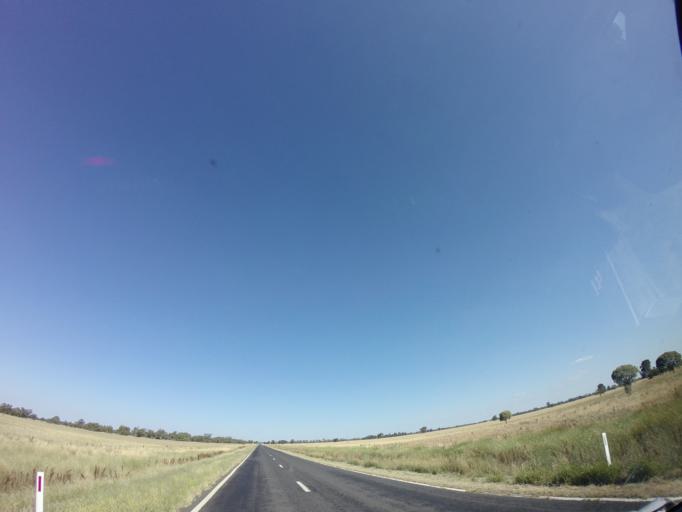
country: AU
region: New South Wales
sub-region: Gilgandra
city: Gilgandra
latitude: -31.6666
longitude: 148.1949
